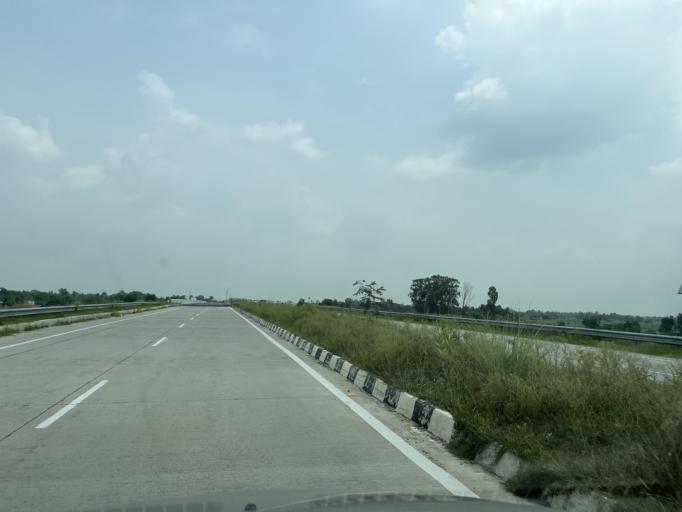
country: IN
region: Uttar Pradesh
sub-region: Bijnor
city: Nagina
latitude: 29.4248
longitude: 78.4277
